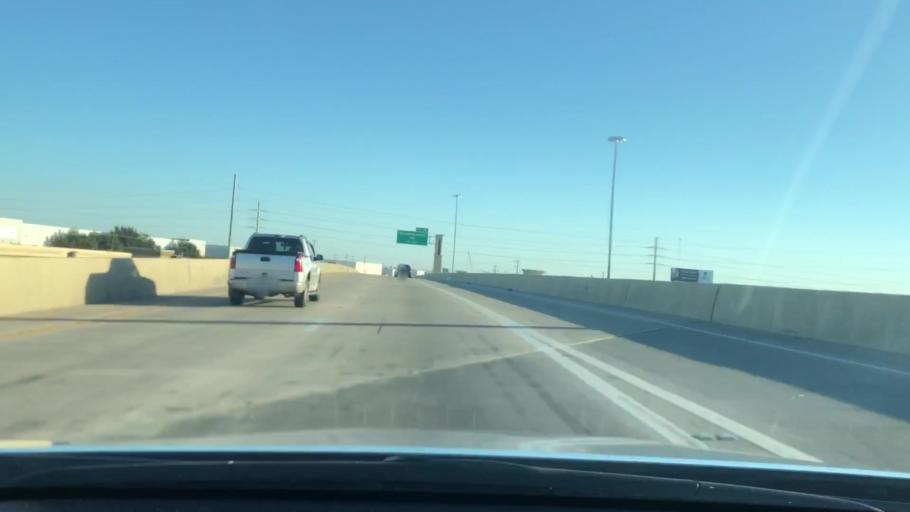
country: US
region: Texas
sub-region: Bexar County
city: Kirby
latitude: 29.4737
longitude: -98.4051
